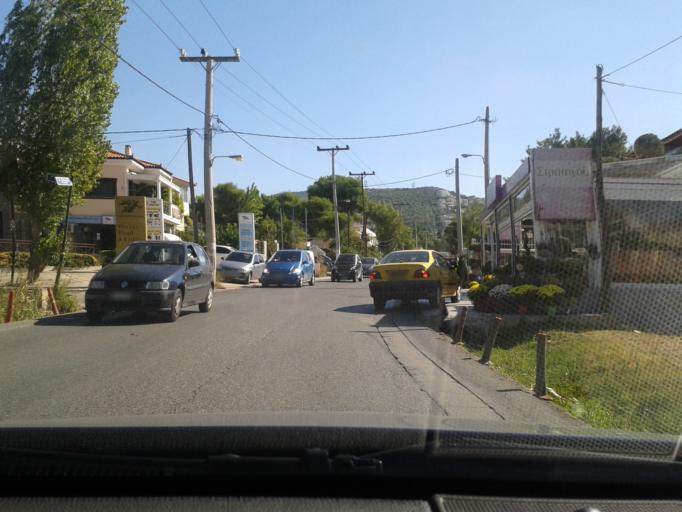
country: GR
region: Attica
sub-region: Nomarchia Athinas
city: Nea Erythraia
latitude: 38.1013
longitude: 23.8173
